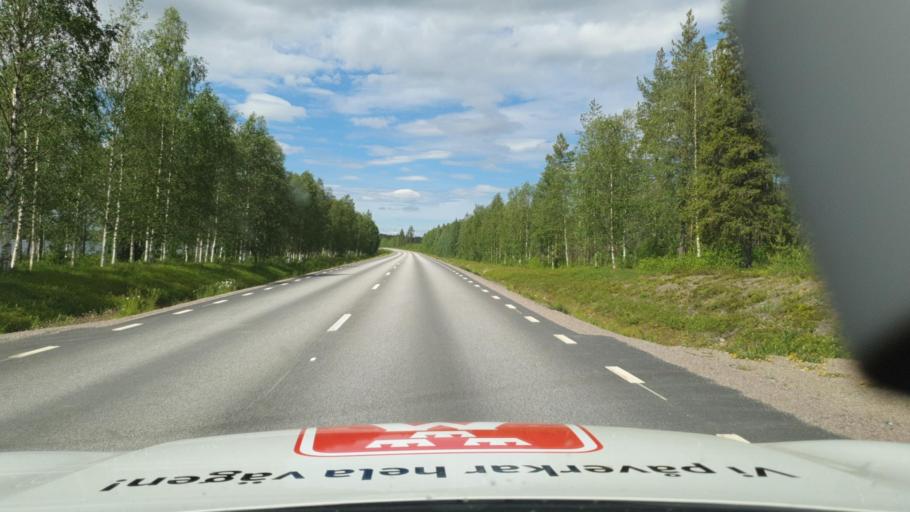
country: SE
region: Vaesterbotten
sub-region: Norsjo Kommun
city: Norsjoe
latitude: 65.1933
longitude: 19.8368
